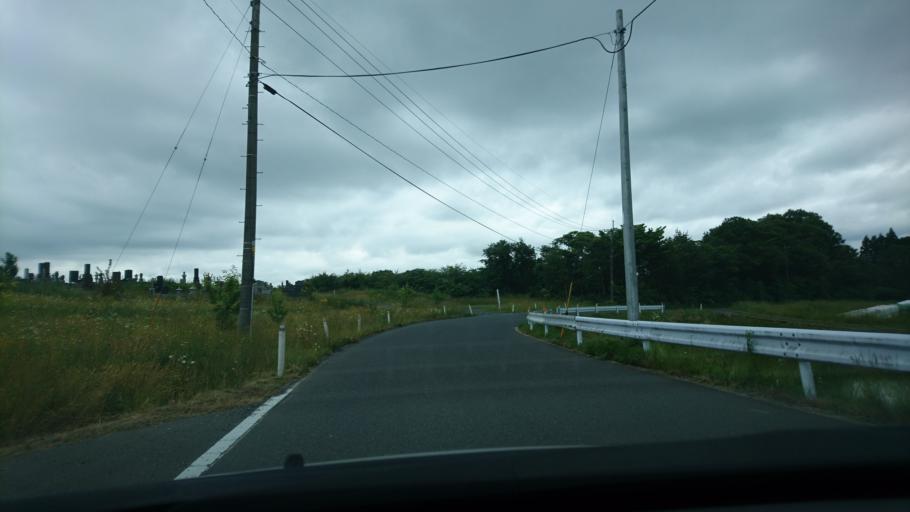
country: JP
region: Iwate
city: Ichinoseki
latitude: 38.8789
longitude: 141.2013
